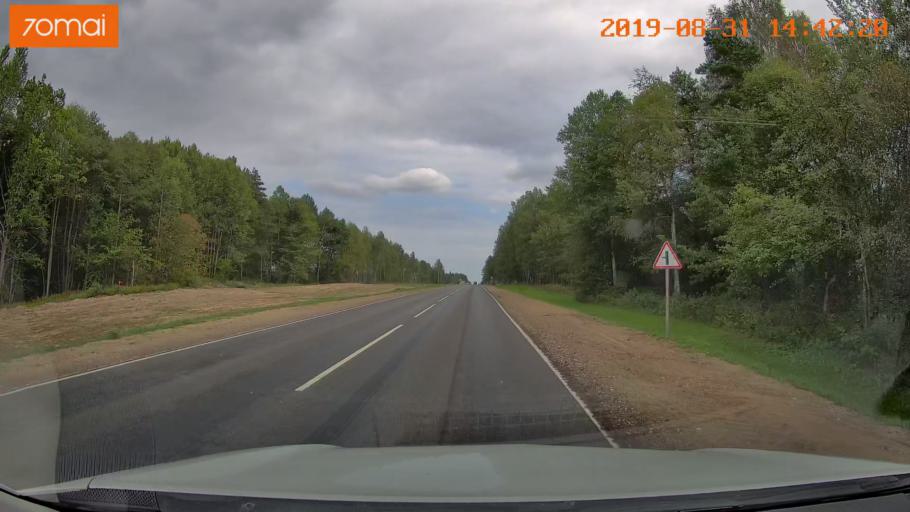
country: RU
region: Smolensk
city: Yekimovichi
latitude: 54.2072
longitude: 33.6056
